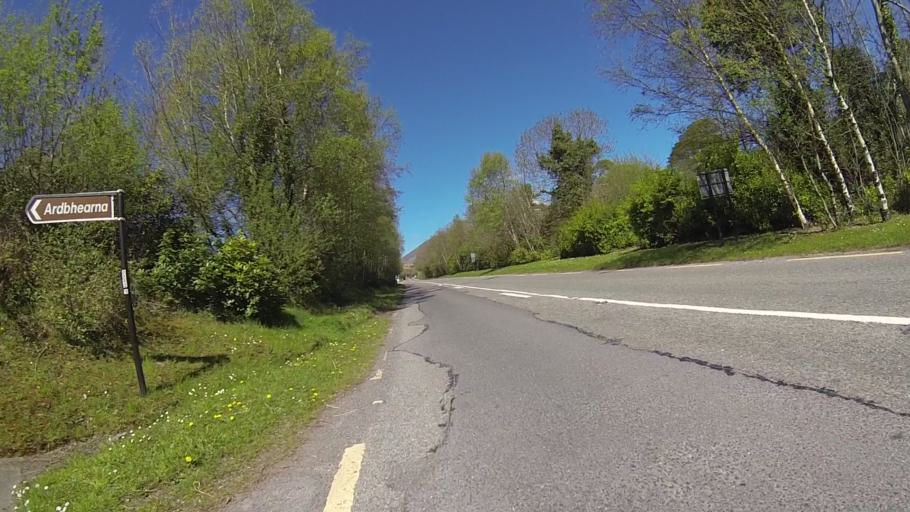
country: IE
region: Munster
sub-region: Ciarrai
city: Kenmare
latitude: 51.8880
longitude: -9.5973
